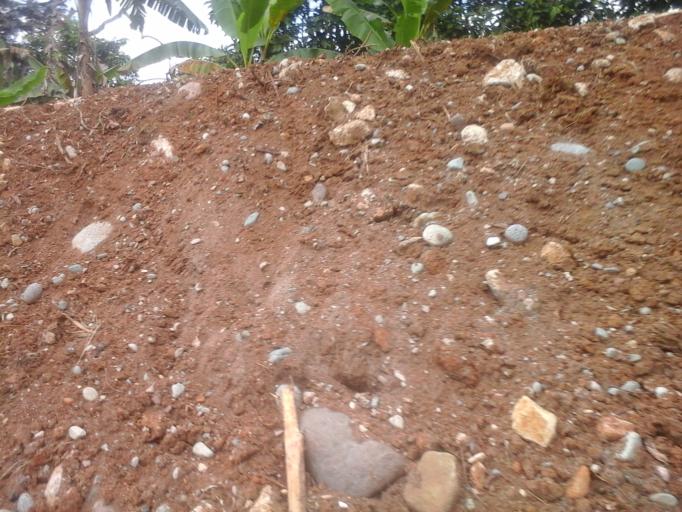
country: CO
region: Putumayo
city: Mocoa
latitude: 1.1751
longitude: -76.6601
